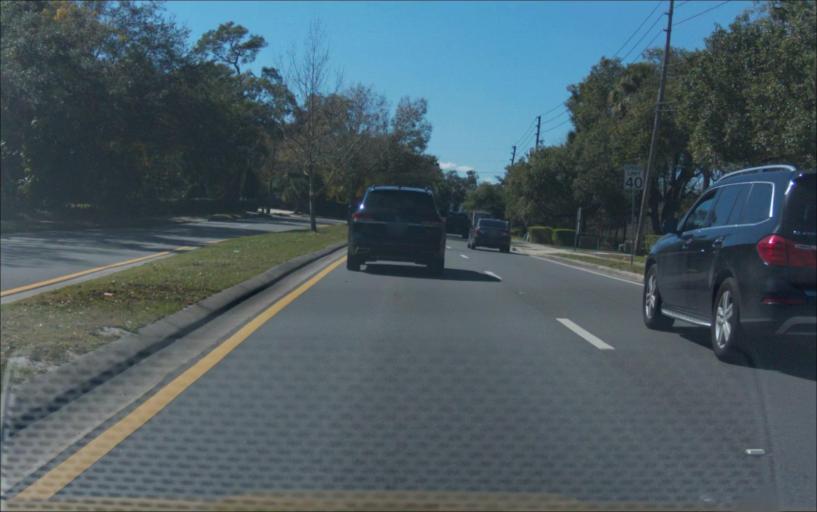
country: US
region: Florida
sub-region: Orange County
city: Winter Park
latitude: 28.6260
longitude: -81.3313
